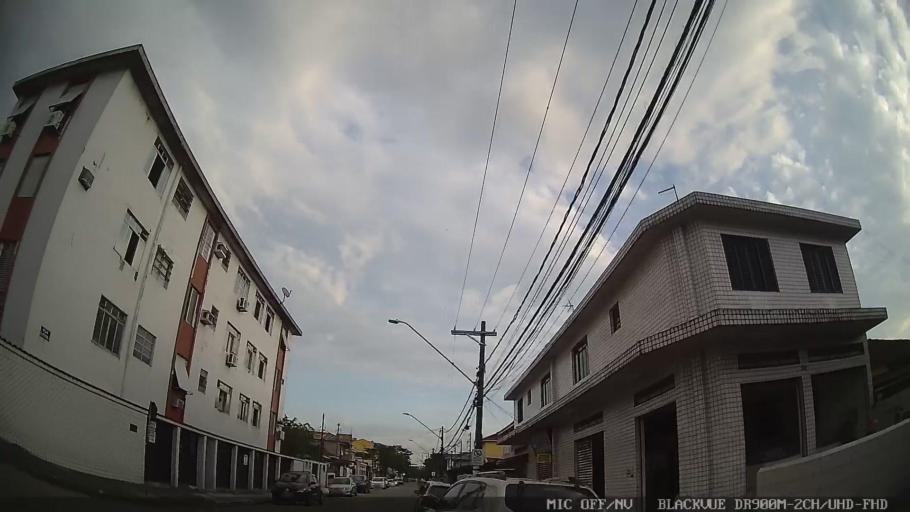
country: BR
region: Sao Paulo
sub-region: Cubatao
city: Cubatao
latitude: -23.8944
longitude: -46.4230
